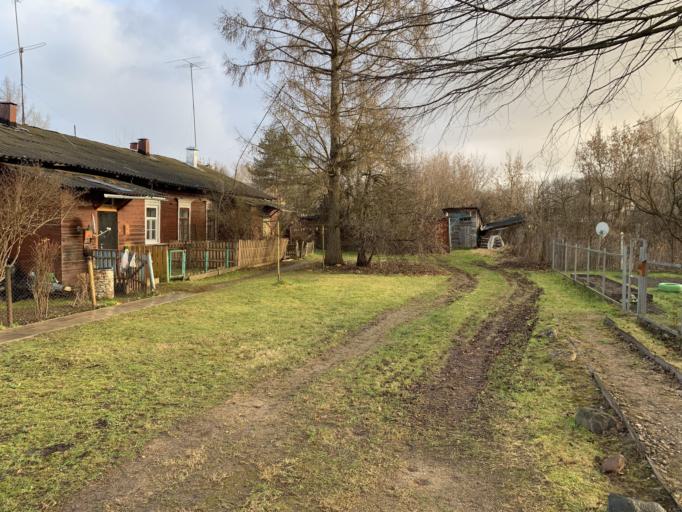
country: RU
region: Tverskaya
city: Likhoslavl'
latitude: 57.1264
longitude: 35.4640
